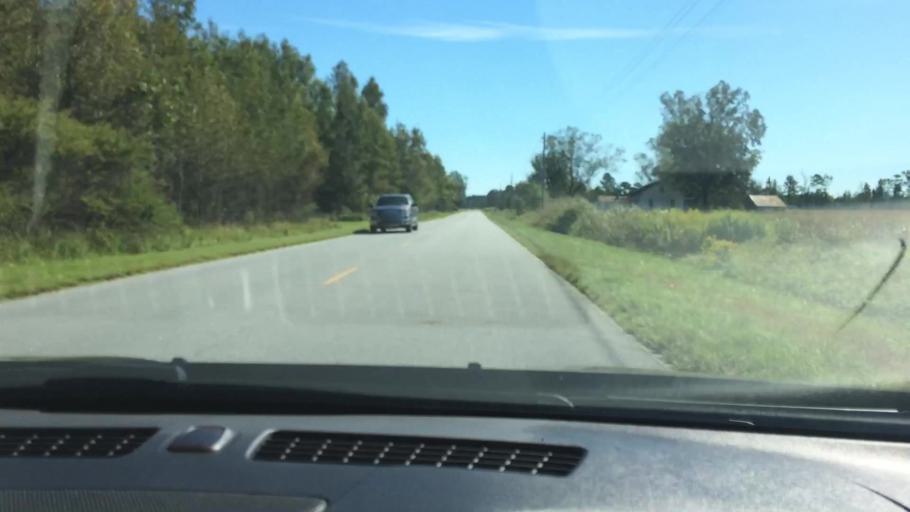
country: US
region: North Carolina
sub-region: Pitt County
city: Grifton
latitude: 35.4036
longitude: -77.4170
